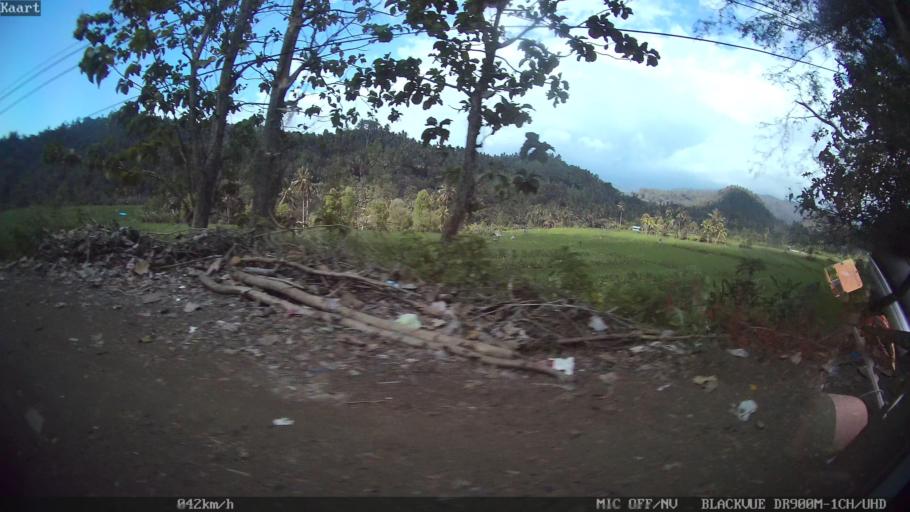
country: ID
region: Bali
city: Kauhan
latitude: -8.2767
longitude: 114.9698
